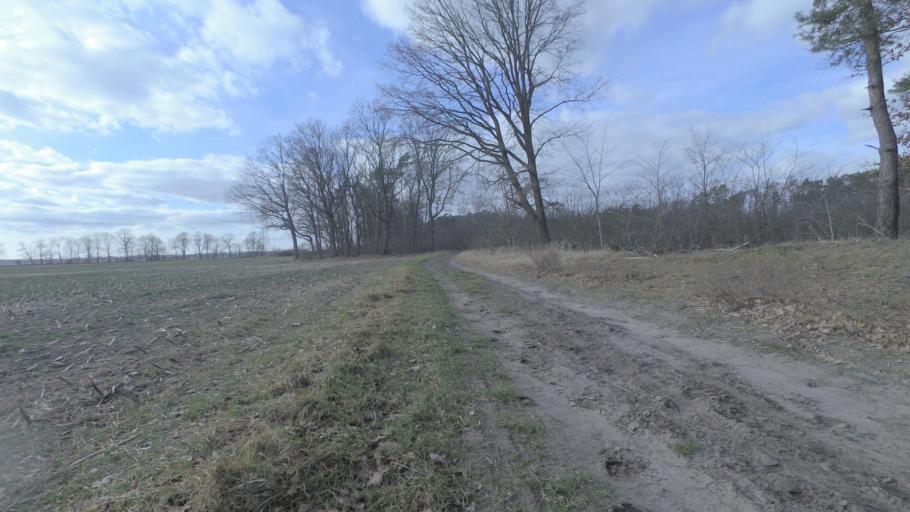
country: DE
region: Brandenburg
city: Trebbin
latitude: 52.2291
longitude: 13.2953
